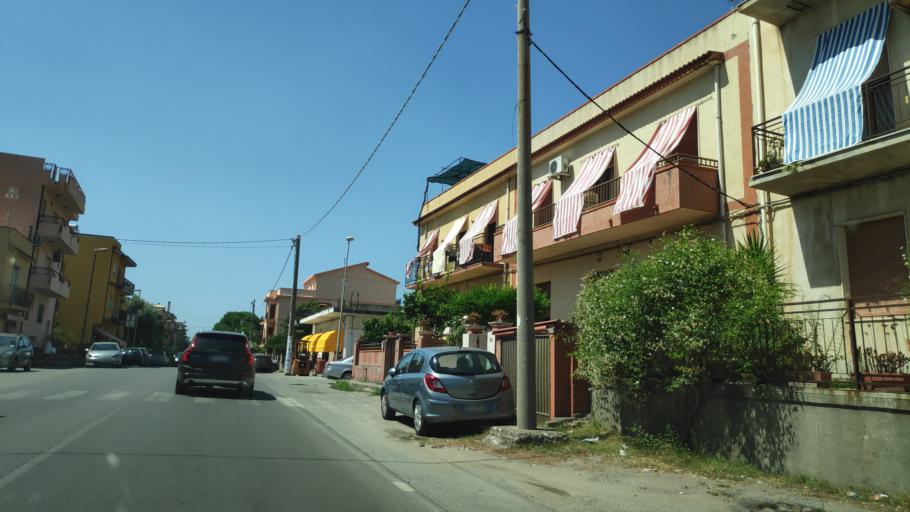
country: IT
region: Calabria
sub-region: Provincia di Reggio Calabria
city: Weather Station
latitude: 37.9616
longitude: 16.0997
